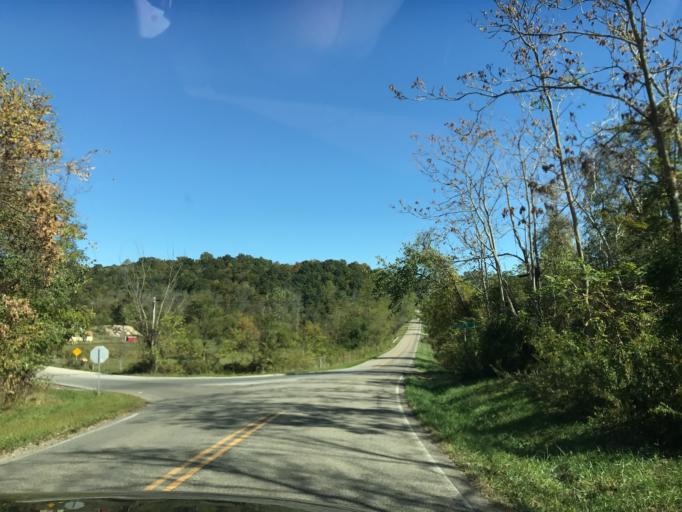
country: US
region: Ohio
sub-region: Guernsey County
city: Byesville
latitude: 40.0245
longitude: -81.5150
